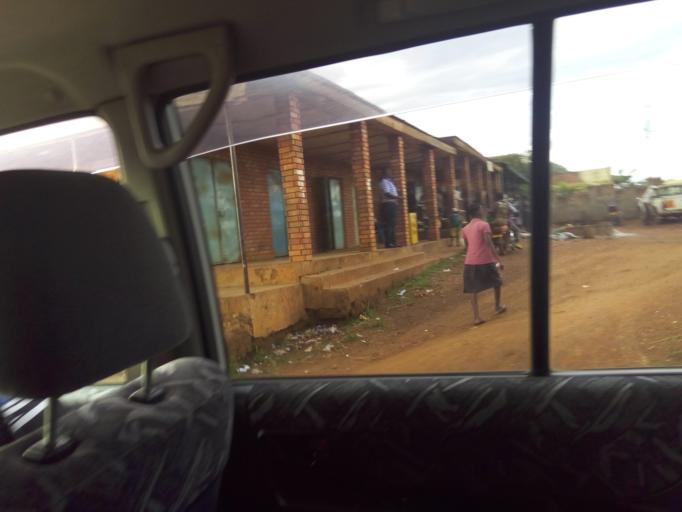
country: UG
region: Western Region
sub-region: Masindi District
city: Masindi
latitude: 1.6816
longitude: 31.7185
